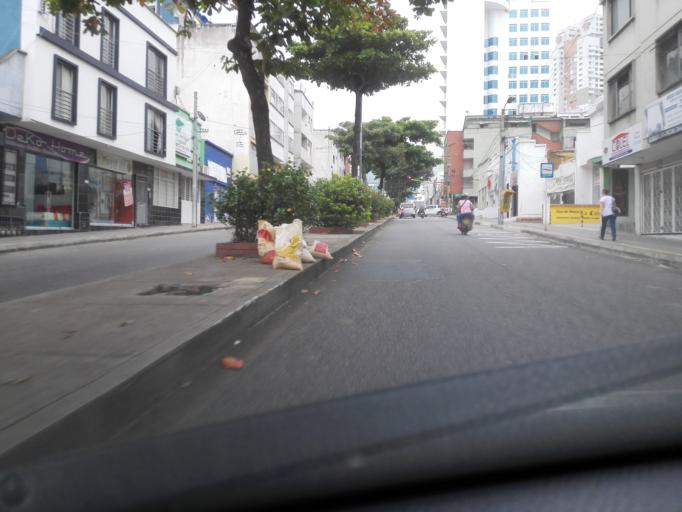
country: CO
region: Santander
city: Bucaramanga
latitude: 7.1205
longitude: -73.1189
